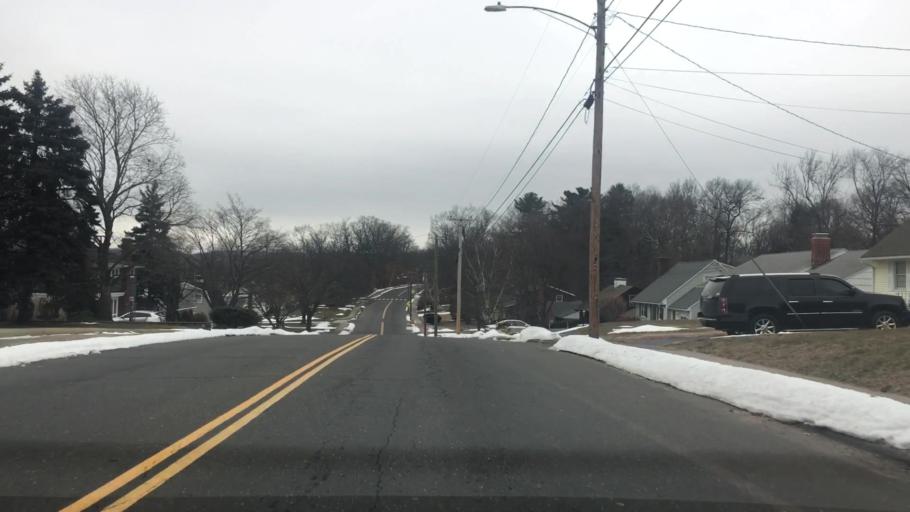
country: US
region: Connecticut
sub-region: Hartford County
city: Bristol
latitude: 41.6830
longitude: -72.9181
